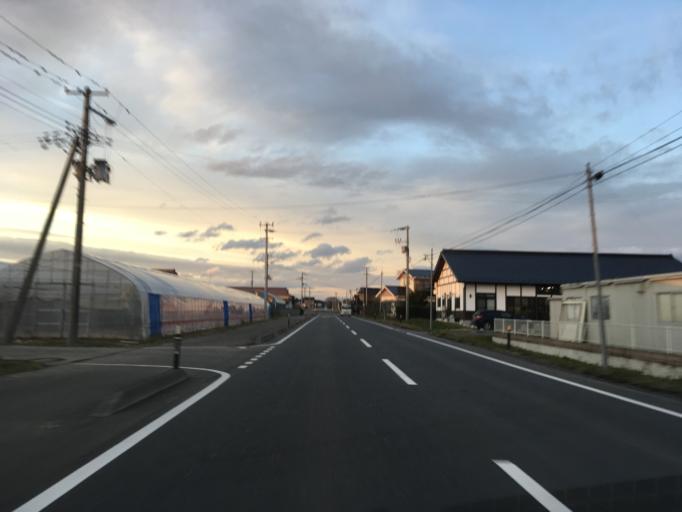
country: JP
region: Miyagi
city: Wakuya
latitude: 38.7135
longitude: 141.2583
